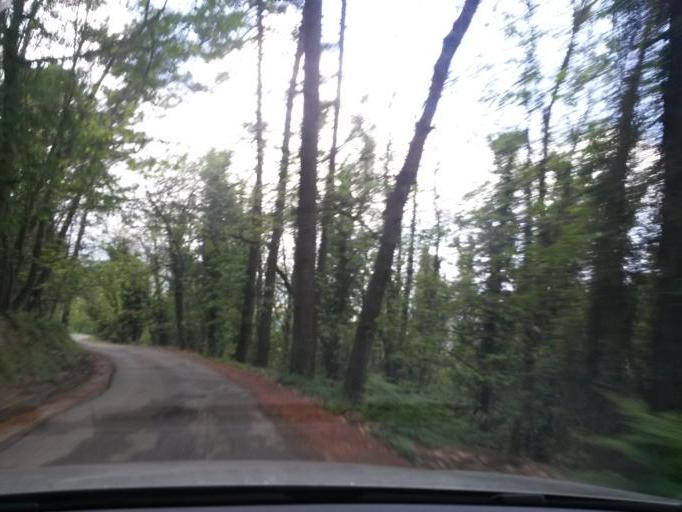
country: IT
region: Tuscany
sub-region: Provincia di Livorno
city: Marciana Marina
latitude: 42.7802
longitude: 10.2015
